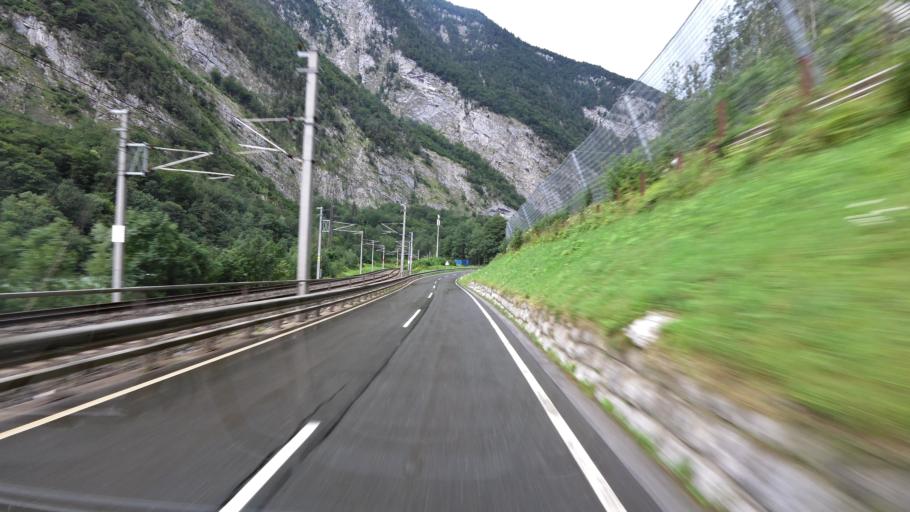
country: AT
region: Salzburg
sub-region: Politischer Bezirk Hallein
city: Golling an der Salzach
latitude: 47.5537
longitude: 13.1687
